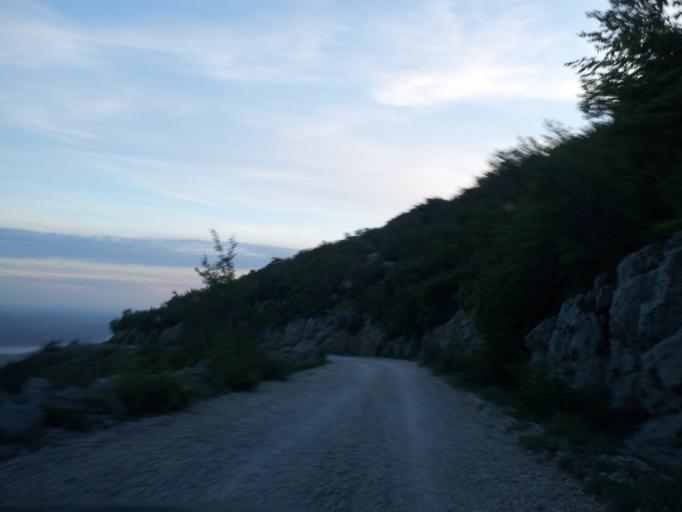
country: HR
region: Zadarska
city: Obrovac
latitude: 44.2548
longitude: 15.6380
